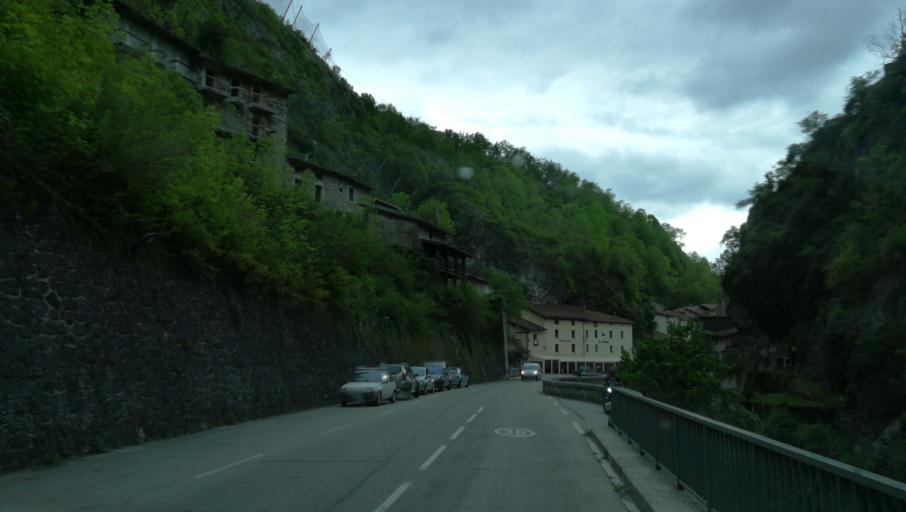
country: FR
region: Rhone-Alpes
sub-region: Departement de l'Isere
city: Pont-en-Royans
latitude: 45.0612
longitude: 5.3482
